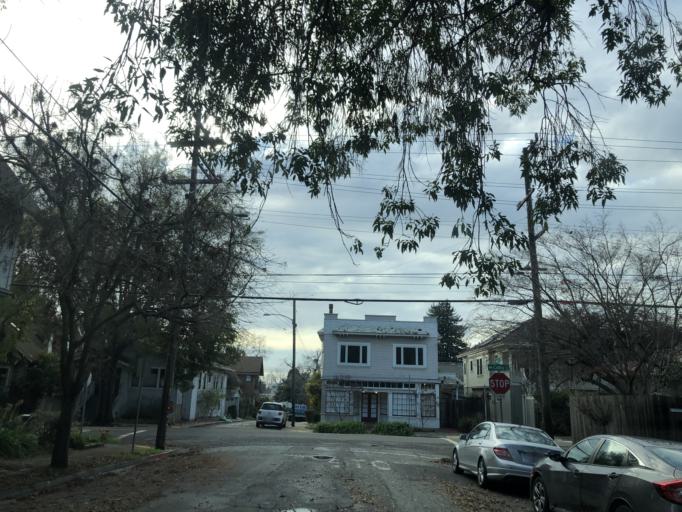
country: US
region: California
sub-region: Alameda County
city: Berkeley
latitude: 37.8479
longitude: -122.2562
